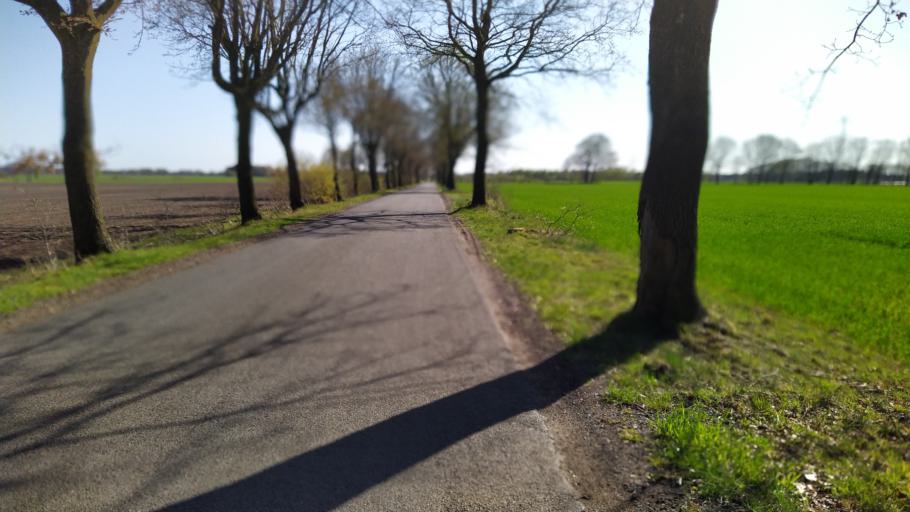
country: DE
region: Lower Saxony
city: Heeslingen
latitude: 53.3212
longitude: 9.3899
